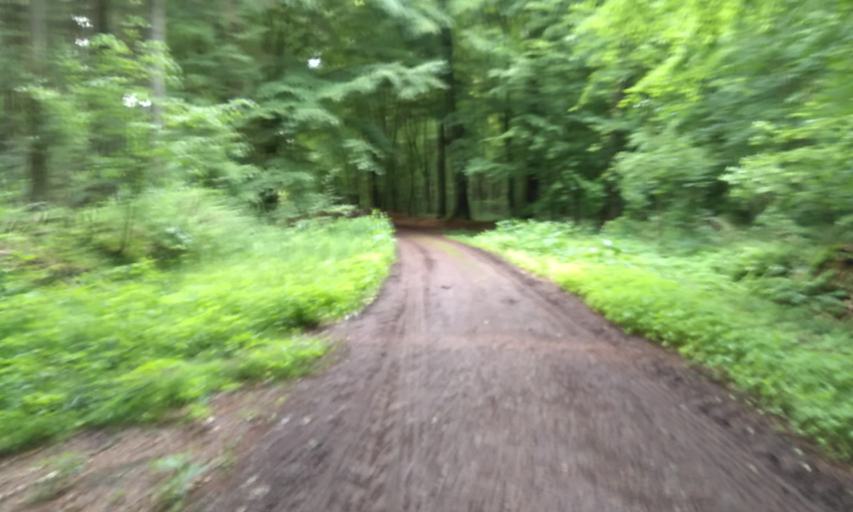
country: DE
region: Lower Saxony
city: Nottensdorf
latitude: 53.4746
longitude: 9.6212
